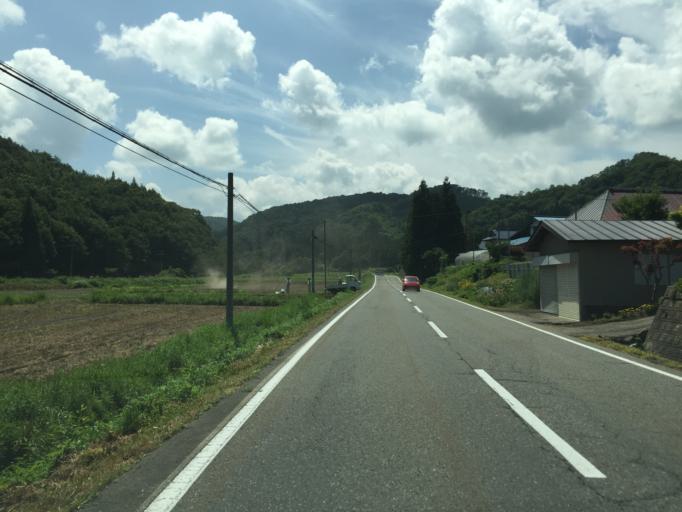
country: JP
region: Fukushima
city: Inawashiro
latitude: 37.4354
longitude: 140.0224
